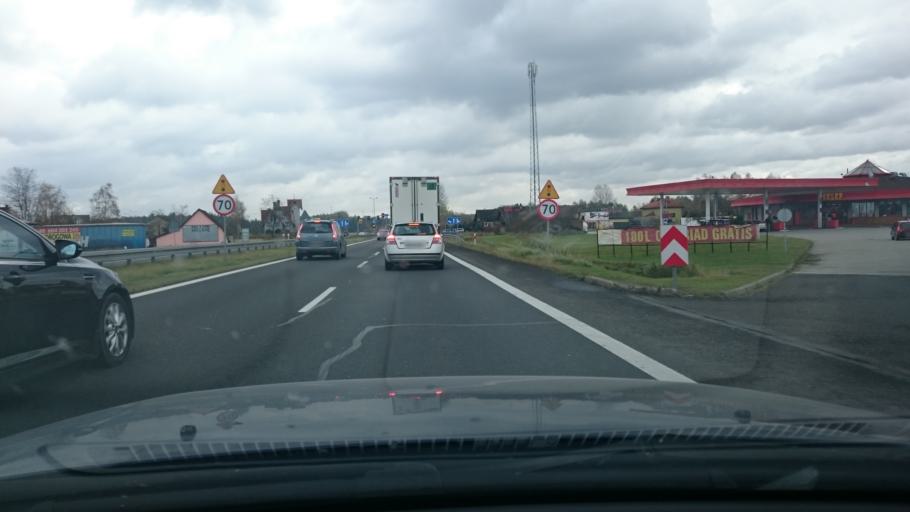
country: PL
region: Lesser Poland Voivodeship
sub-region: Powiat olkuski
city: Boleslaw
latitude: 50.3062
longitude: 19.4771
